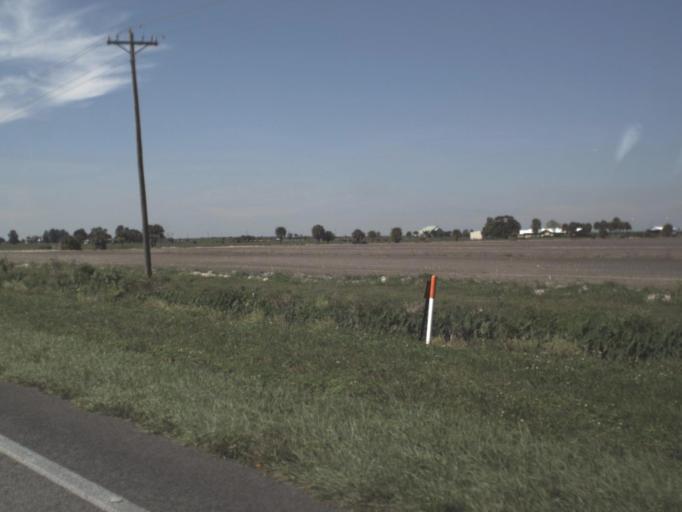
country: US
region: Florida
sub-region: Hendry County
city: Harlem
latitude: 26.7542
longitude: -81.0050
